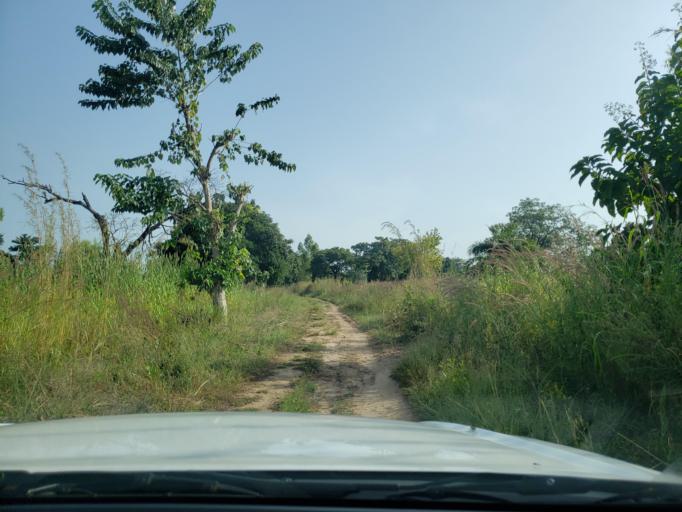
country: TG
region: Kara
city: Bafilo
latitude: 9.4093
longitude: 1.1758
